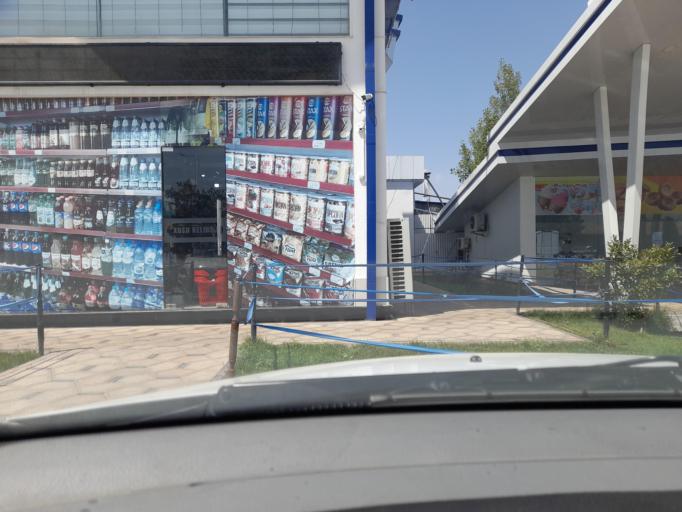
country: UZ
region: Samarqand
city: Bulung'ur
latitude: 39.7704
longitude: 67.2692
